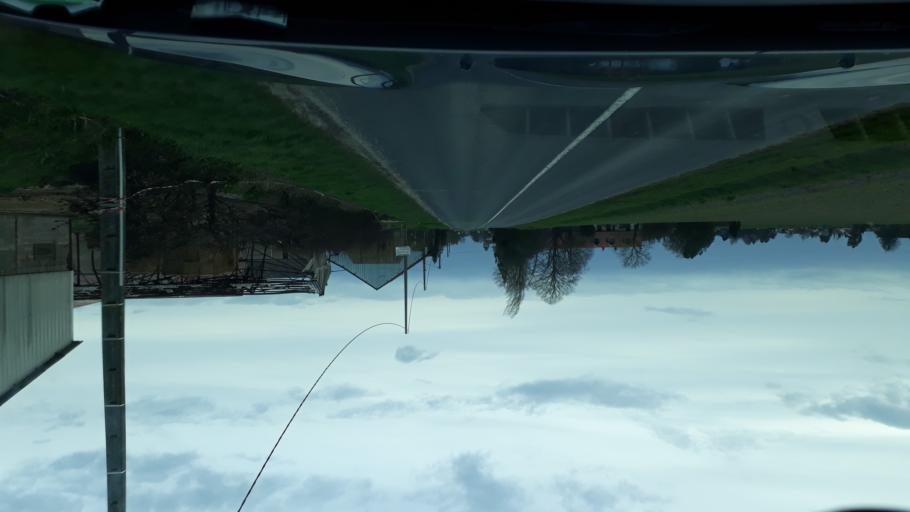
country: FR
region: Centre
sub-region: Departement du Loiret
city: Chilleurs-aux-Bois
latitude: 48.0664
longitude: 2.1472
